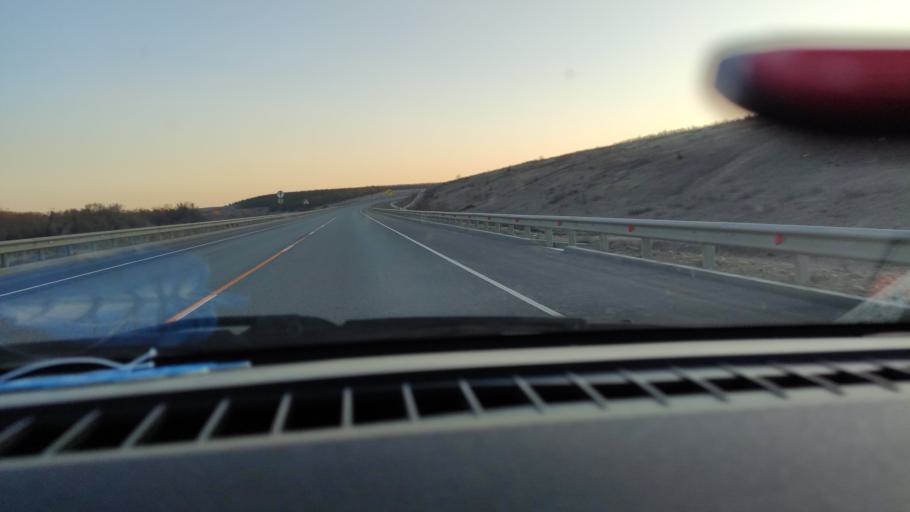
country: RU
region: Saratov
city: Yelshanka
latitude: 51.8697
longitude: 46.5041
